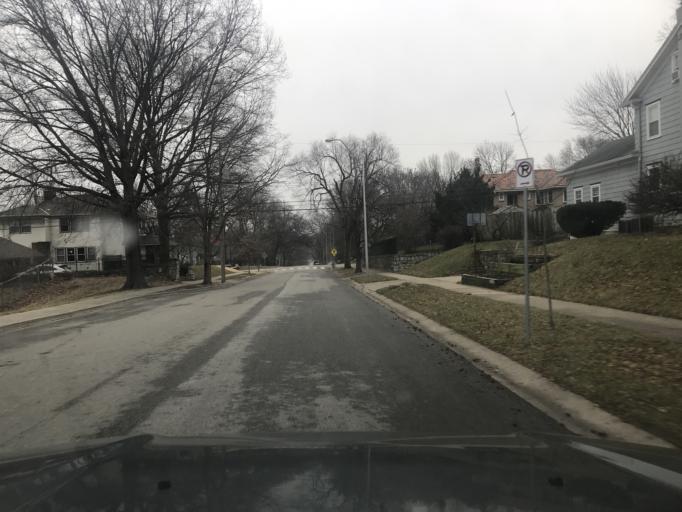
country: US
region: Kansas
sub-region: Johnson County
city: Mission Hills
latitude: 39.0242
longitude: -94.5914
